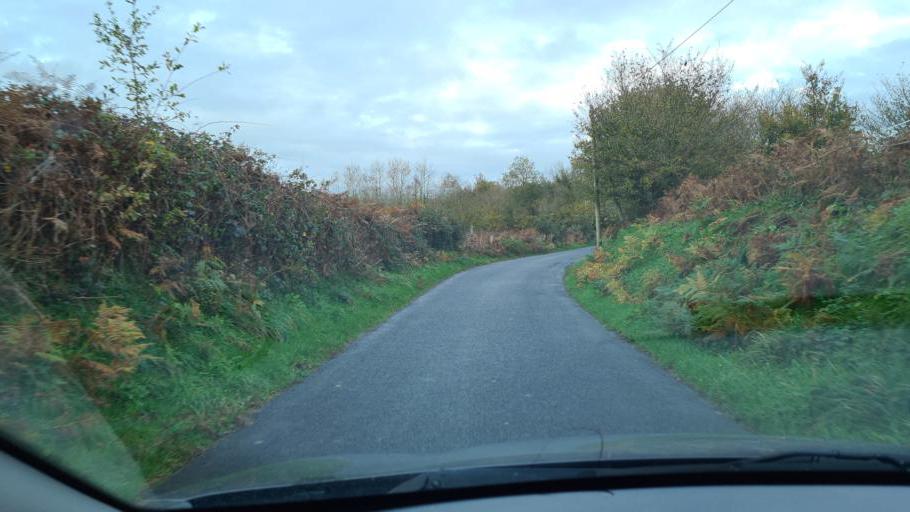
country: FR
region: Lower Normandy
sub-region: Departement de la Manche
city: La Haye-Pesnel
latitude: 48.7850
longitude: -1.4020
